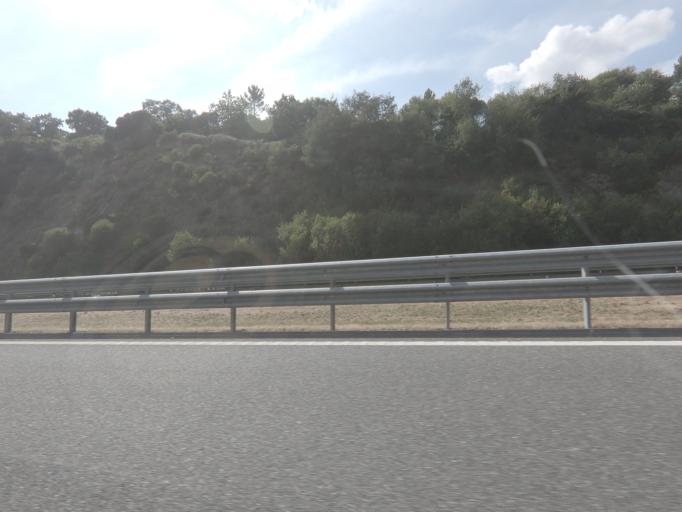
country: ES
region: Galicia
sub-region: Provincia de Ourense
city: Cenlle
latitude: 42.3306
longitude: -8.0744
